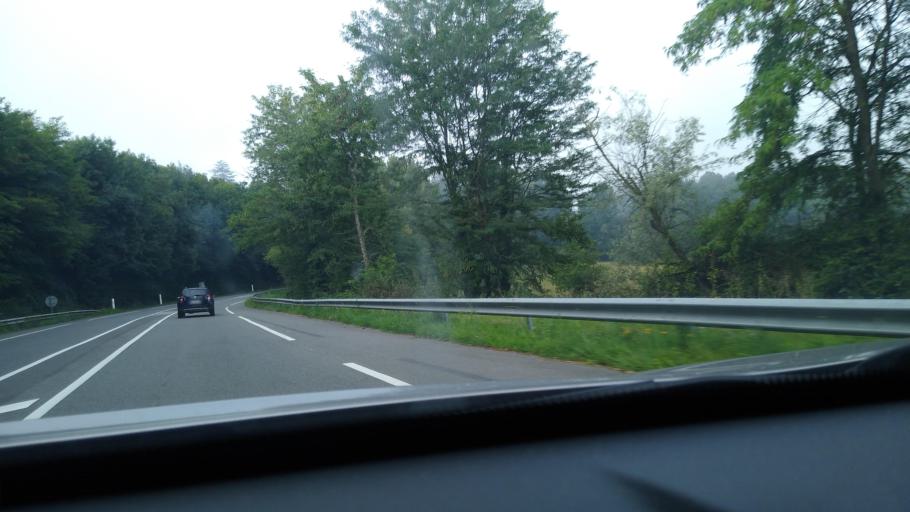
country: FR
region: Midi-Pyrenees
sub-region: Departement de la Haute-Garonne
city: Salies-du-Salat
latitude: 43.1217
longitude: 0.9356
